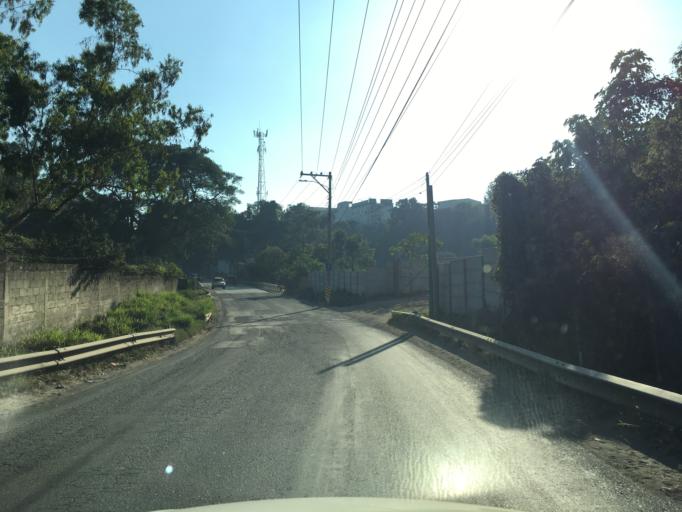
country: GT
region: Guatemala
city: Villa Nueva
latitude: 14.5355
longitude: -90.6160
